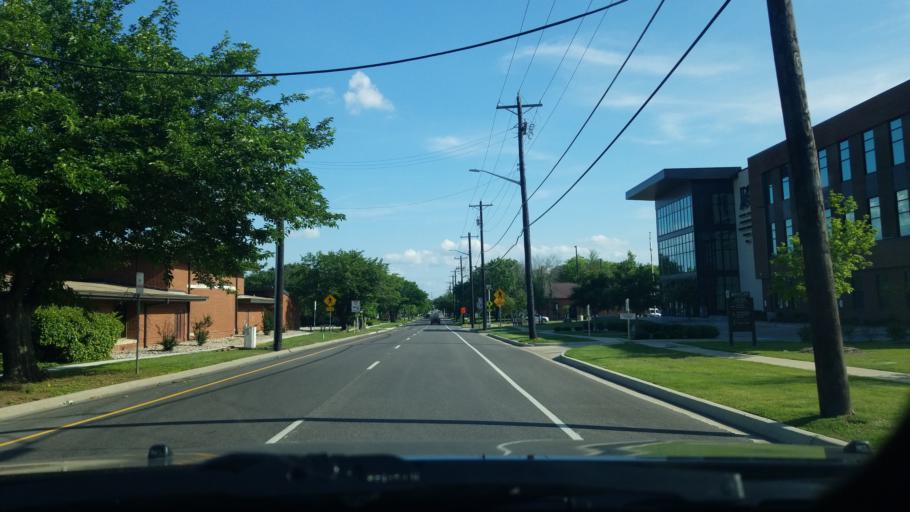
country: US
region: Texas
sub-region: Denton County
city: Denton
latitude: 33.2260
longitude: -97.1336
